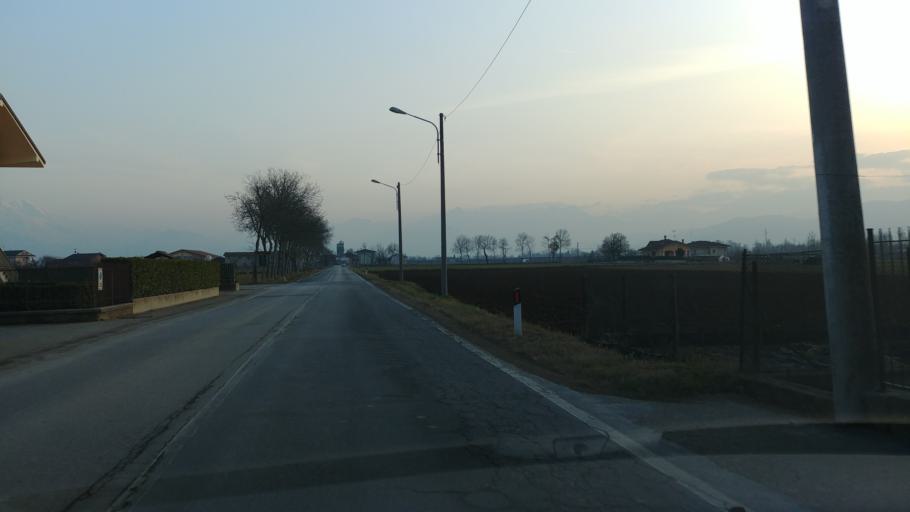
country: IT
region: Piedmont
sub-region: Provincia di Cuneo
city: Roata Rossi
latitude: 44.4280
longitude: 7.5066
